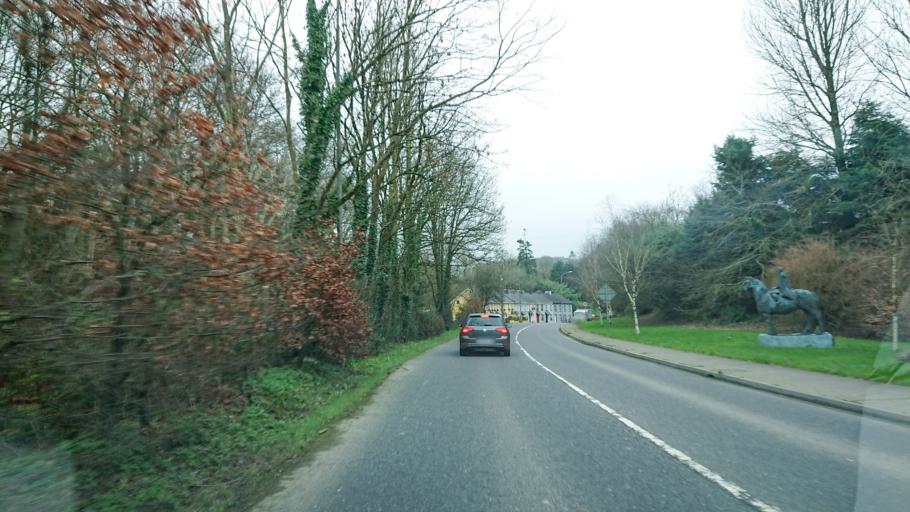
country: IE
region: Munster
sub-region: County Cork
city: Bandon
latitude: 51.7654
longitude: -8.6526
